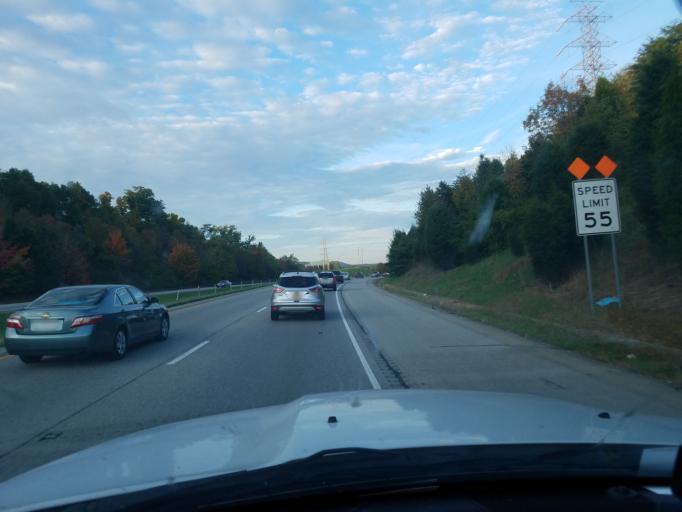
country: US
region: Indiana
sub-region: Floyd County
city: New Albany
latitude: 38.3069
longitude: -85.8495
